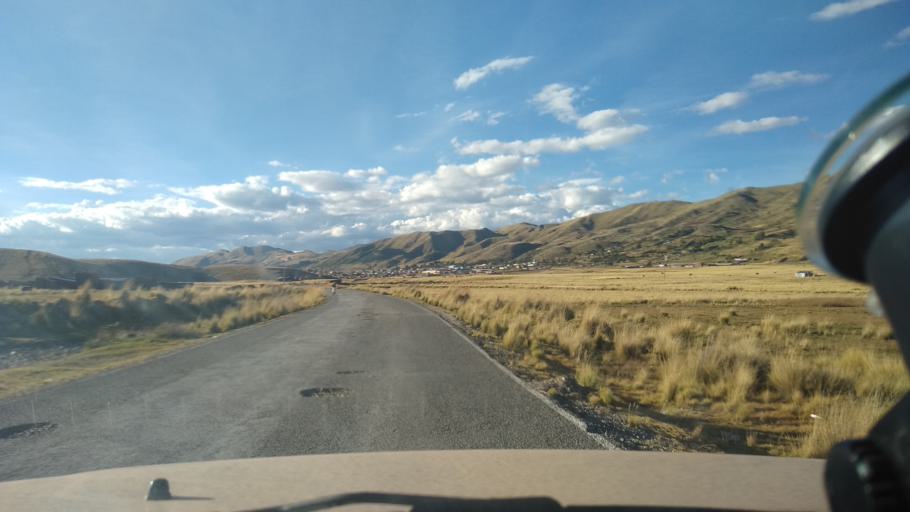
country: PE
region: Cusco
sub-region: Provincia de Canas
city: Chignayhua
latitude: -14.2382
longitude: -71.4326
